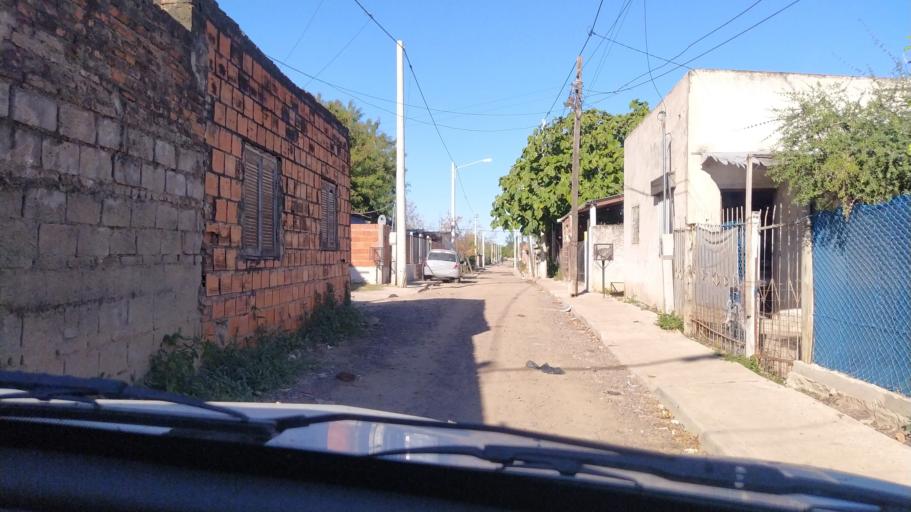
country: AR
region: Corrientes
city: Corrientes
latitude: -27.4940
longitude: -58.8060
